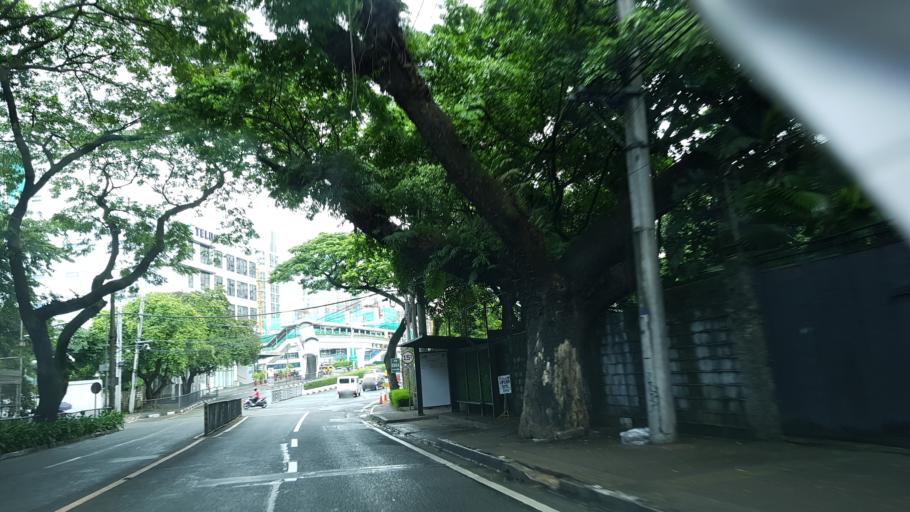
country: PH
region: Metro Manila
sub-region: Makati City
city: Makati City
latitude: 14.5493
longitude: 121.0307
